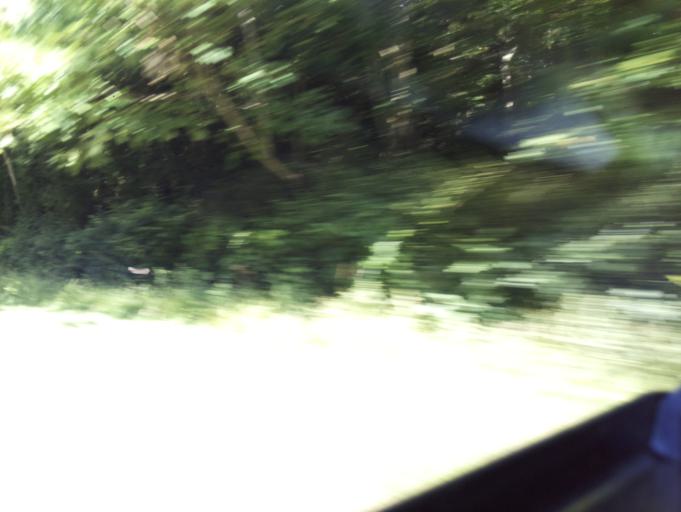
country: GB
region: England
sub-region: Oxfordshire
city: Shrivenham
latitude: 51.6432
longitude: -1.6500
